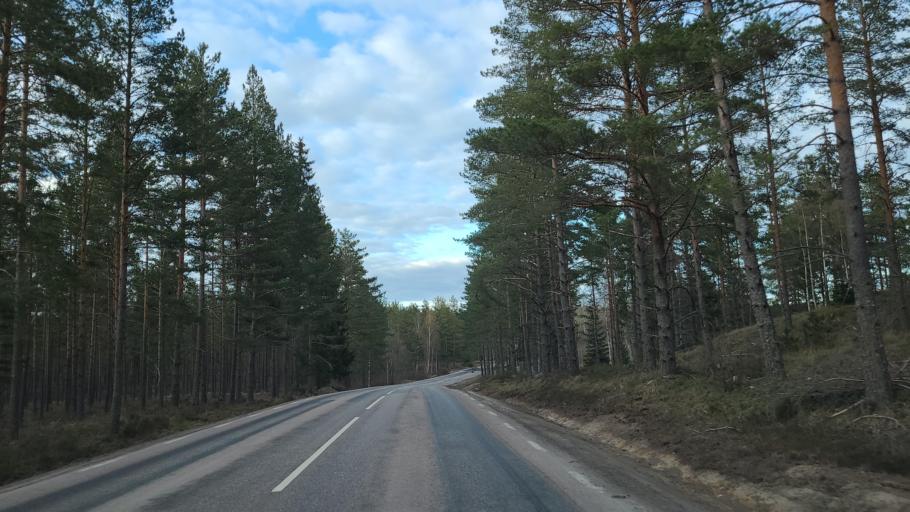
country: SE
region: Soedermanland
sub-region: Nykopings Kommun
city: Olstorp
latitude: 58.7194
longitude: 16.6579
